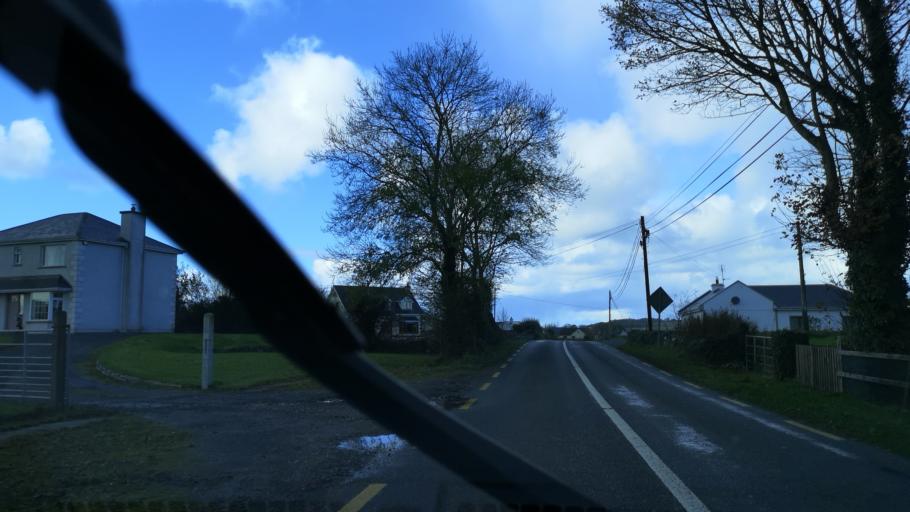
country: IE
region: Connaught
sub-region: Maigh Eo
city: Westport
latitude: 53.7790
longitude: -9.4307
